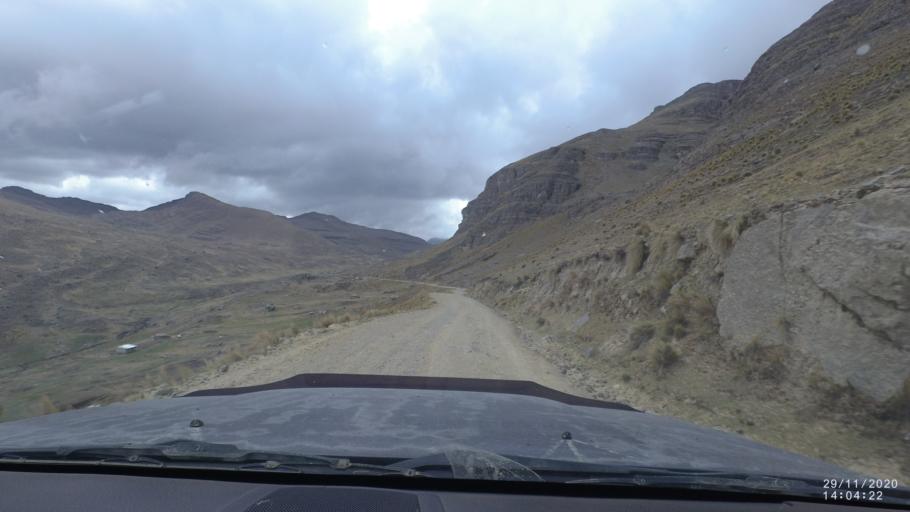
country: BO
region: Cochabamba
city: Sipe Sipe
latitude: -17.2002
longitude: -66.3765
